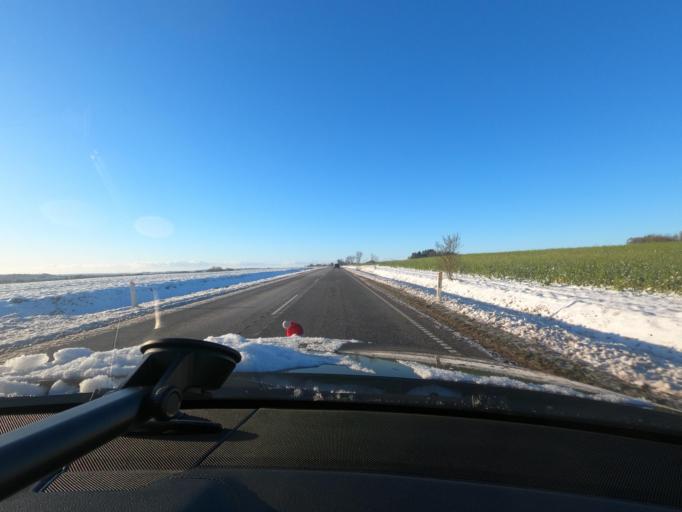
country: DK
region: South Denmark
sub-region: Tonder Kommune
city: Toftlund
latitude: 55.1786
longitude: 9.0507
